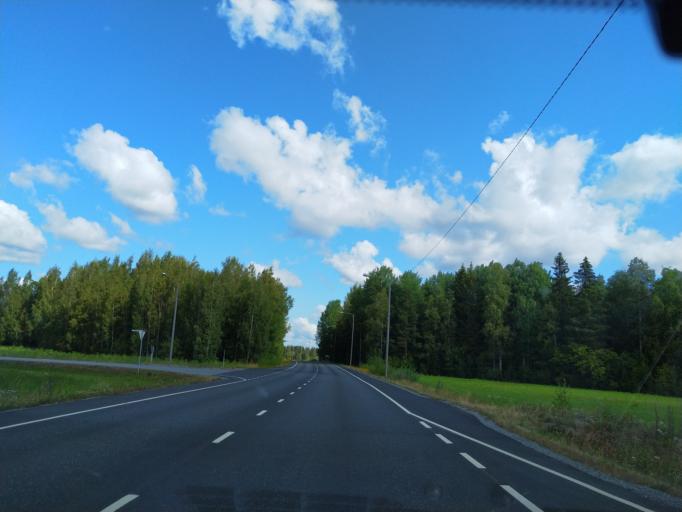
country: FI
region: Satakunta
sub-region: Pori
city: Huittinen
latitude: 61.1749
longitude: 22.7109
